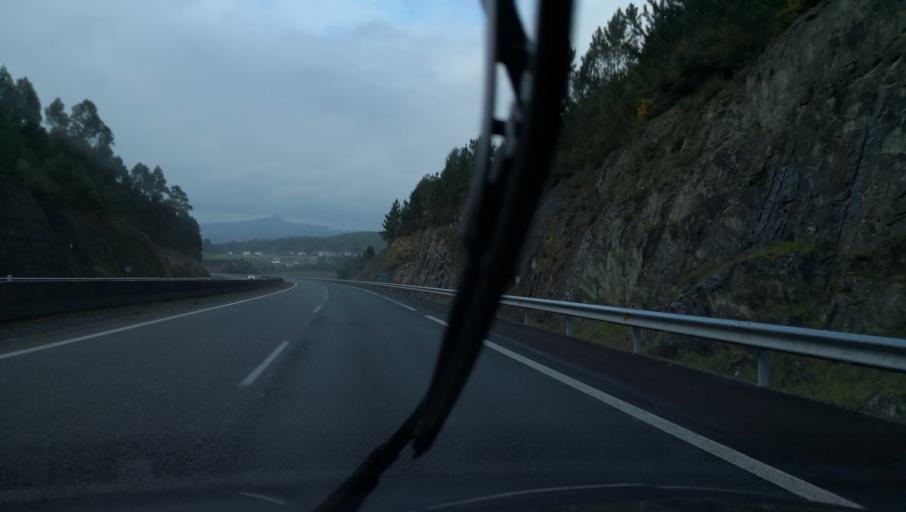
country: ES
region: Galicia
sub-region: Provincia da Coruna
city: Ribeira
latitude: 42.7410
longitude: -8.3709
